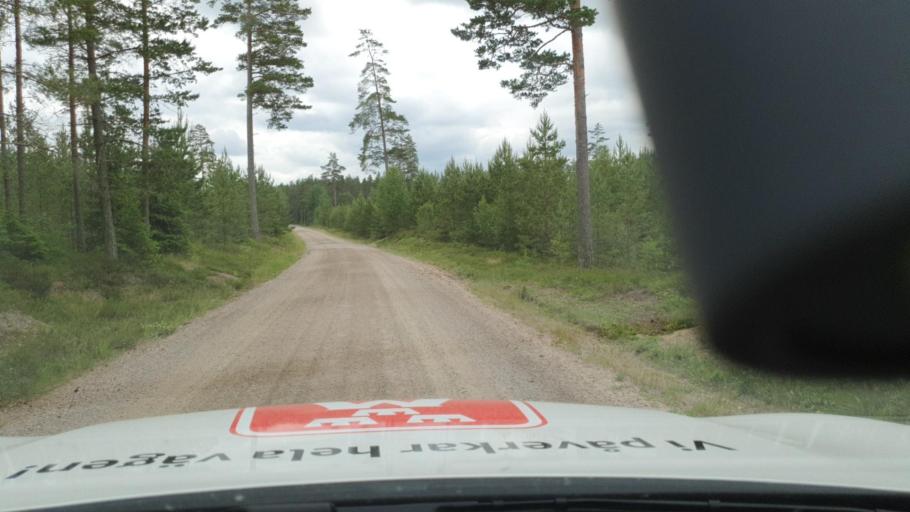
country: SE
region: Vaestra Goetaland
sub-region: Tidaholms Kommun
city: Olofstorp
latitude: 58.1998
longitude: 14.1095
